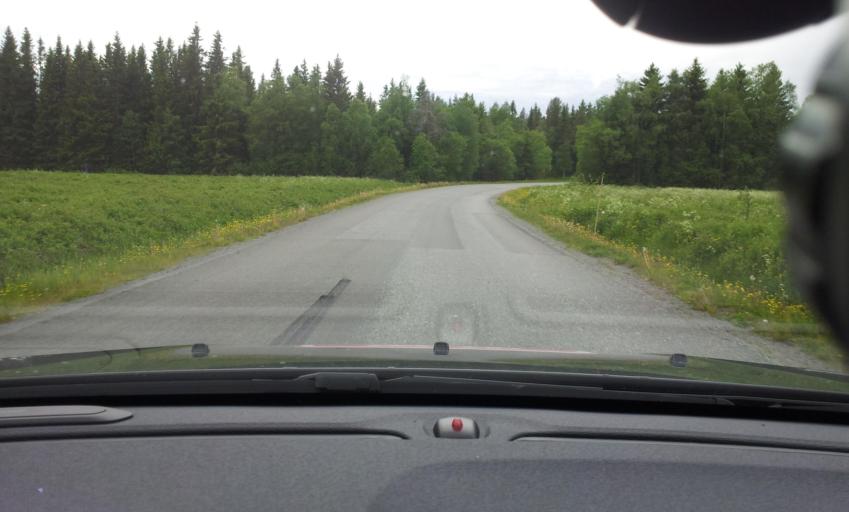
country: SE
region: Jaemtland
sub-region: OEstersunds Kommun
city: Brunflo
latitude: 63.0743
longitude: 14.8564
